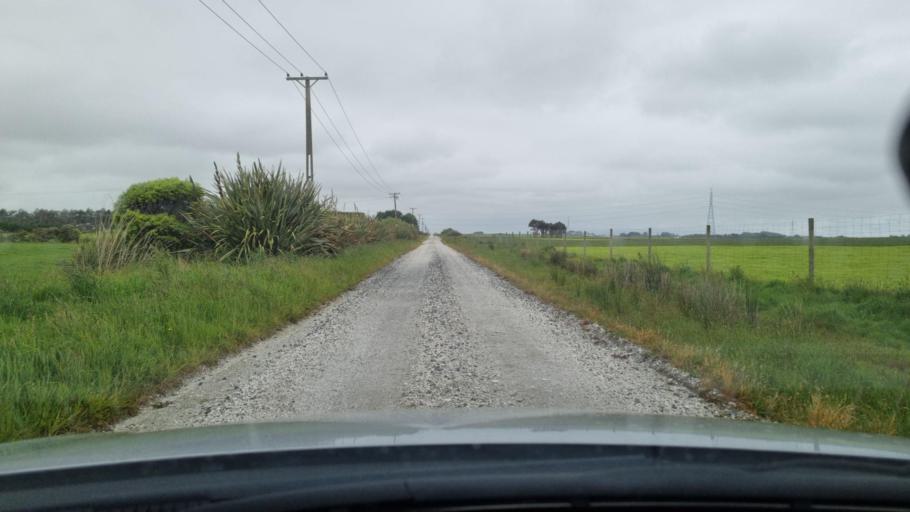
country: NZ
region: Southland
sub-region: Invercargill City
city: Invercargill
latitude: -46.4426
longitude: 168.4335
